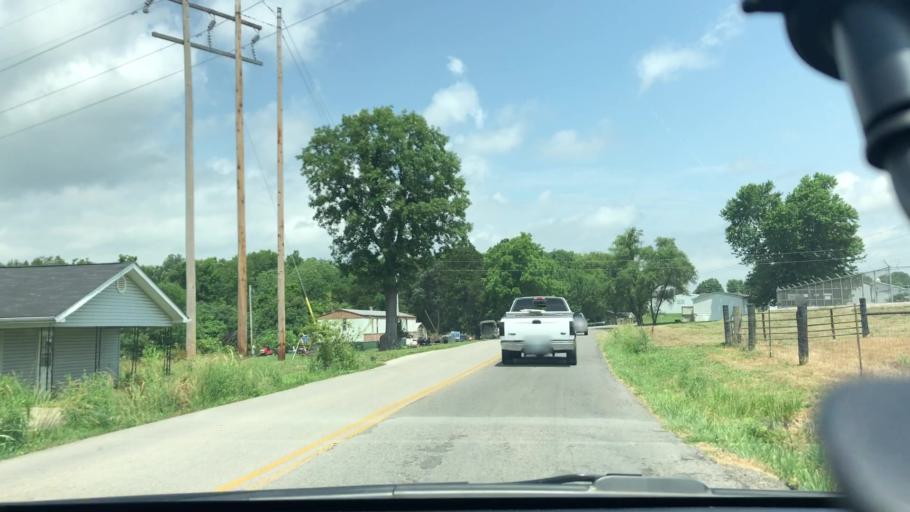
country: US
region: Kentucky
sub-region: Pulaski County
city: Somerset
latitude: 37.0601
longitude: -84.6731
